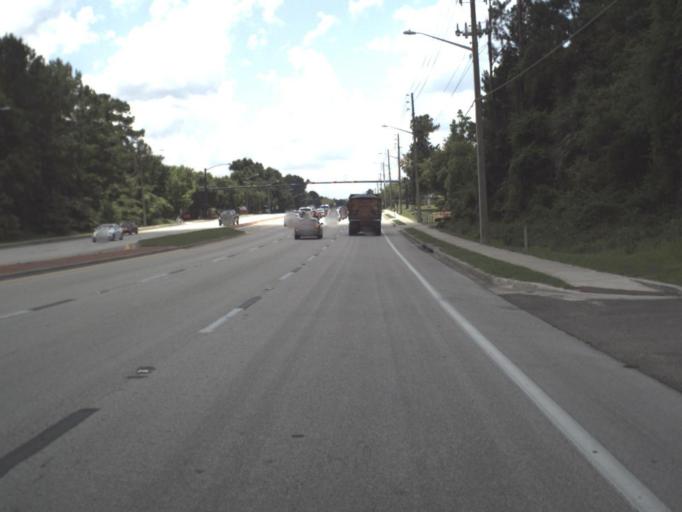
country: US
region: Florida
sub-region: Alachua County
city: Gainesville
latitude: 29.6198
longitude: -82.3728
